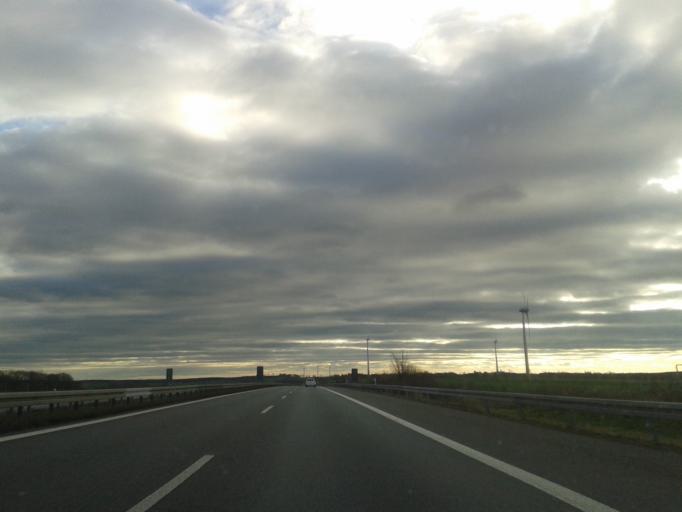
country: DE
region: Saxony
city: Wachau
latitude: 51.1662
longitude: 13.9210
